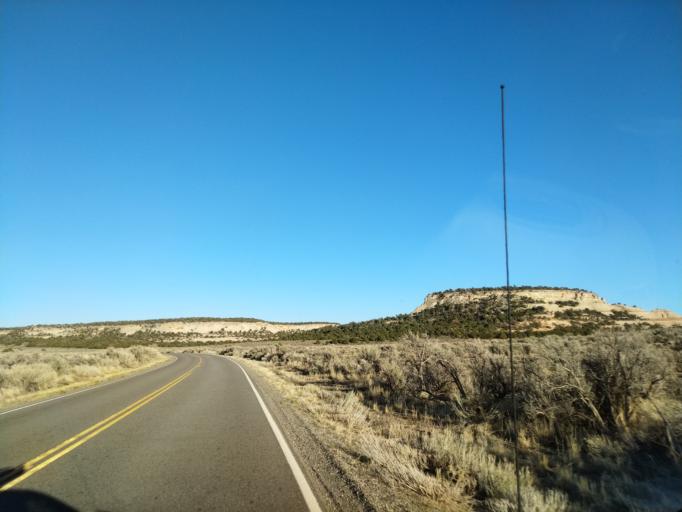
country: US
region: Colorado
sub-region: Mesa County
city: Fruita
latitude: 38.9838
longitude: -108.8080
